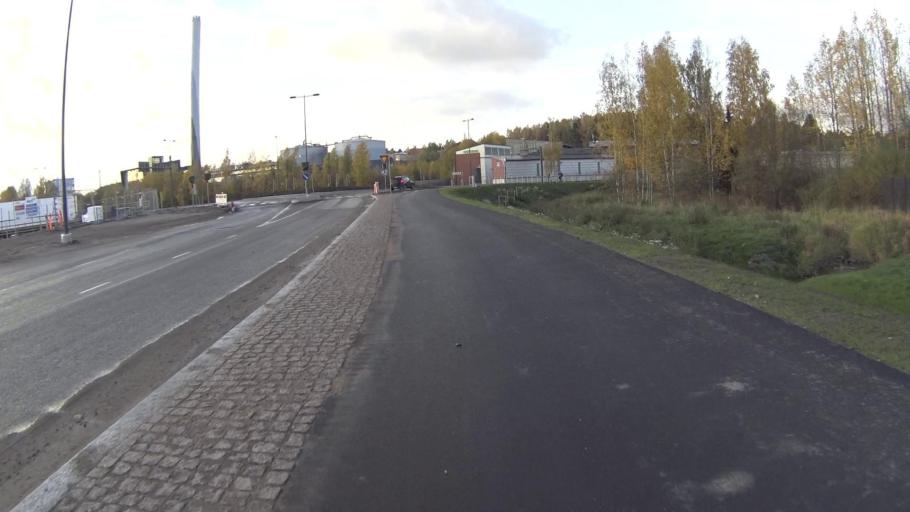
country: FI
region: Uusimaa
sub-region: Helsinki
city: Teekkarikylae
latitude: 60.2164
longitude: 24.8347
